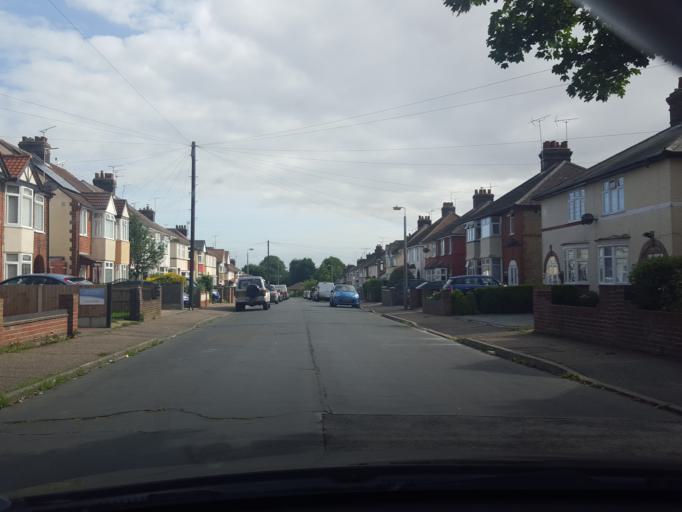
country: GB
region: England
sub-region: Essex
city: Dovercourt
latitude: 51.9343
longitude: 1.2653
